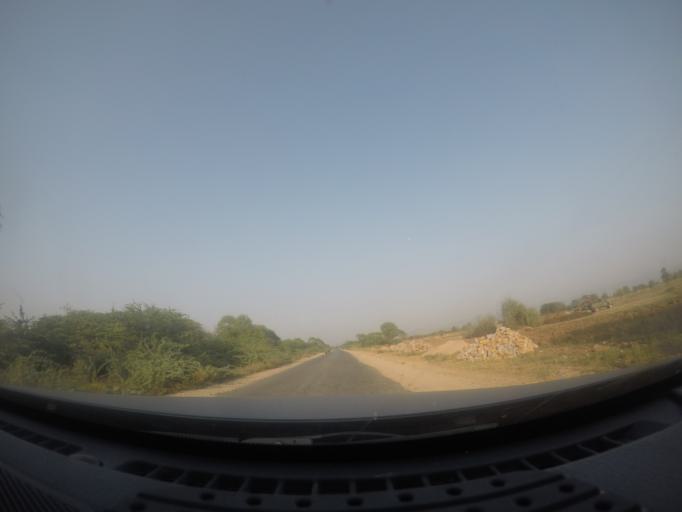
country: MM
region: Mandalay
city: Yamethin
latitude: 20.6659
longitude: 96.1257
